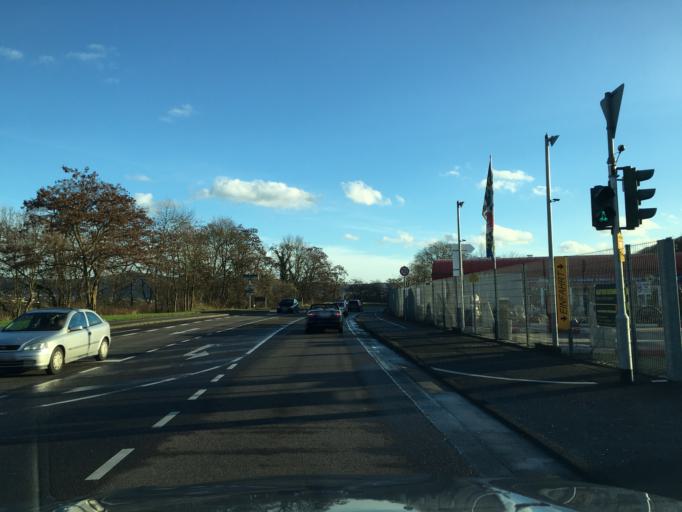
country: DE
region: North Rhine-Westphalia
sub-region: Regierungsbezirk Koln
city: Bad Honnef
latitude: 50.6522
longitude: 7.1979
